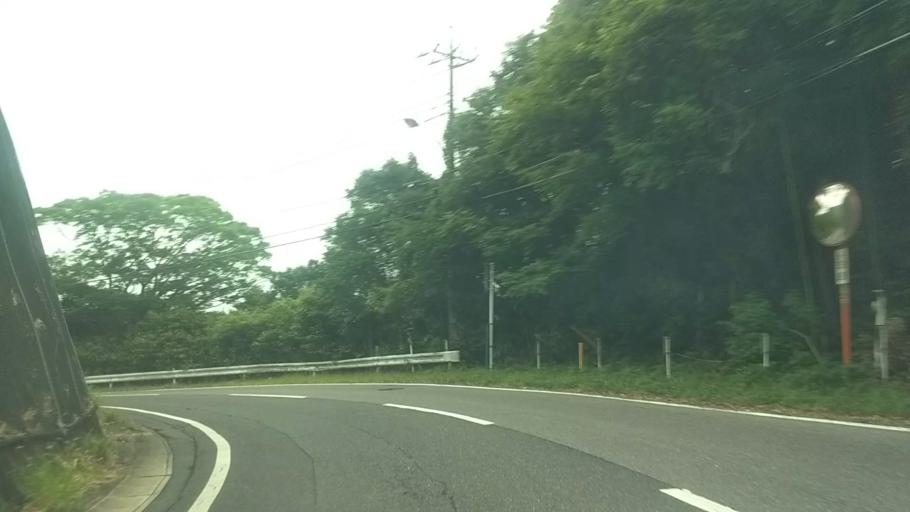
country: JP
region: Chiba
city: Kimitsu
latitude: 35.2312
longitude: 140.0048
